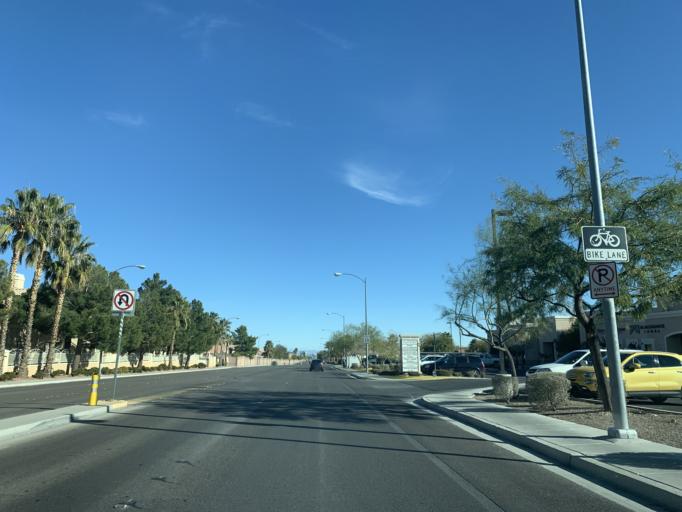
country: US
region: Nevada
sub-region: Clark County
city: Summerlin South
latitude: 36.1225
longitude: -115.3144
